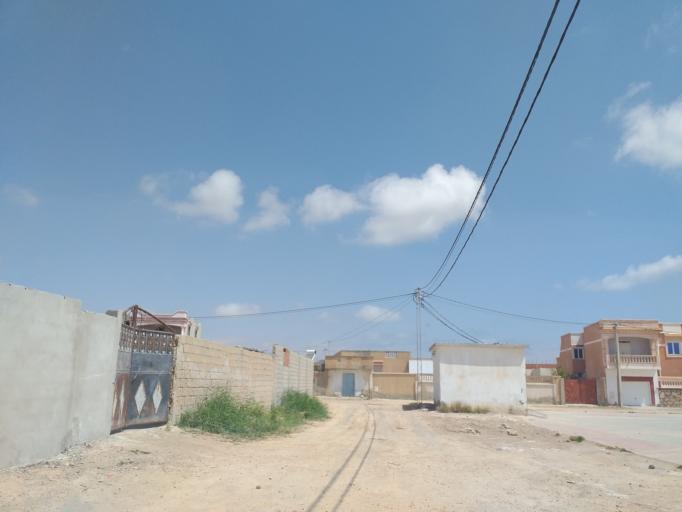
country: TN
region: Qabis
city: Gabes
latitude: 33.9466
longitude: 10.0595
